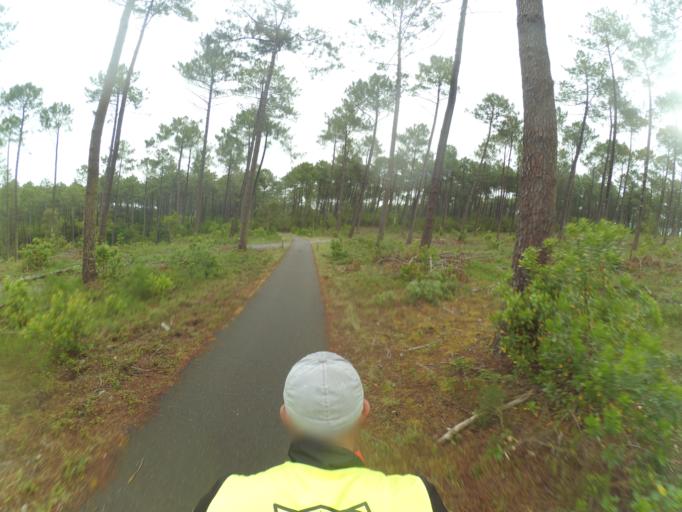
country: FR
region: Aquitaine
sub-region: Departement des Landes
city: Mimizan
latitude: 44.2206
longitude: -1.2508
